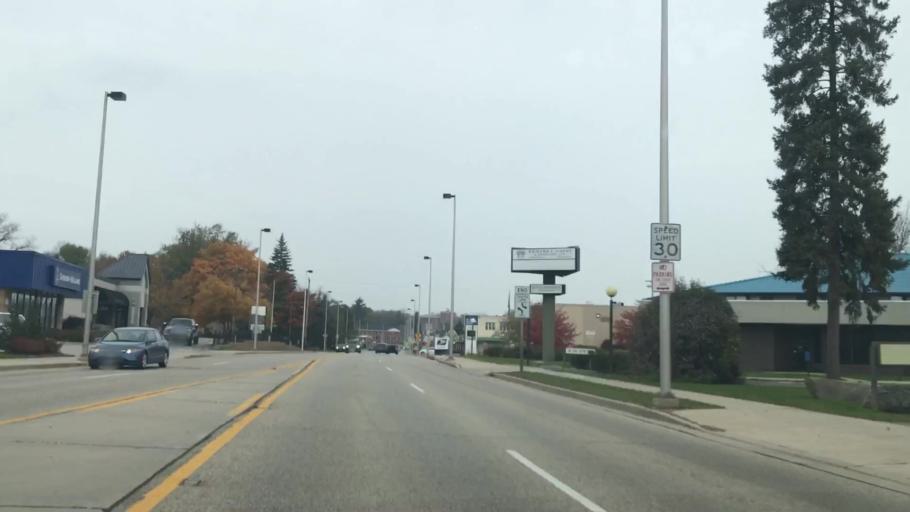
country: US
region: Wisconsin
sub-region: Waukesha County
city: Menomonee Falls
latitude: 43.1724
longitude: -88.1089
